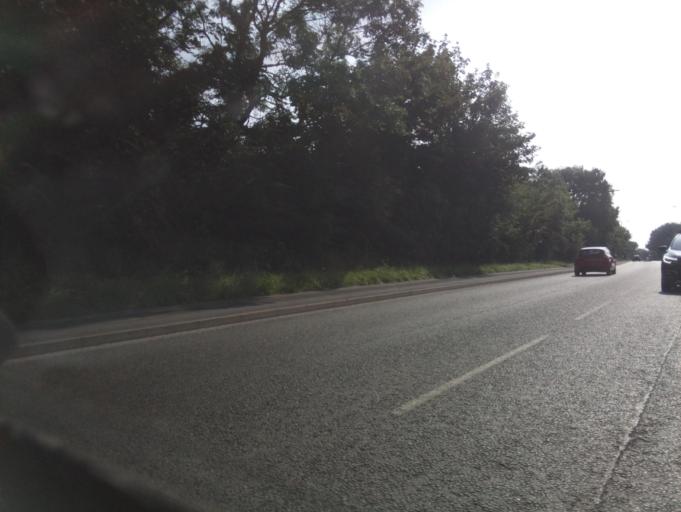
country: GB
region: England
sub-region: Walsall
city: Brownhills
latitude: 52.6345
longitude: -1.9151
